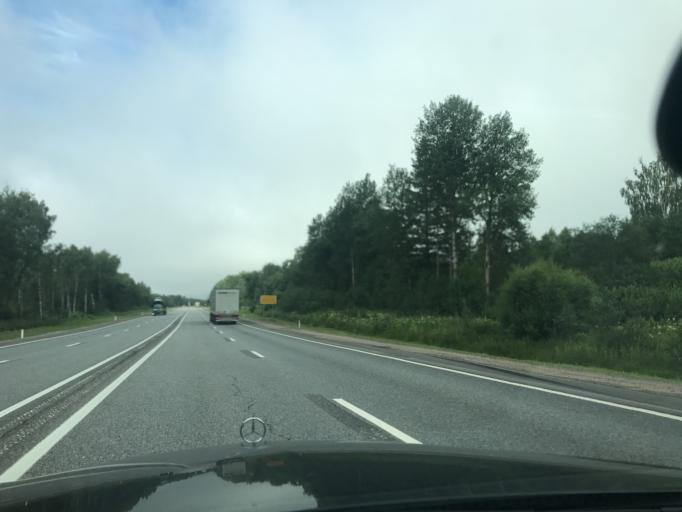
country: RU
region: Smolensk
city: Vyaz'ma
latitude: 55.3292
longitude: 34.5744
